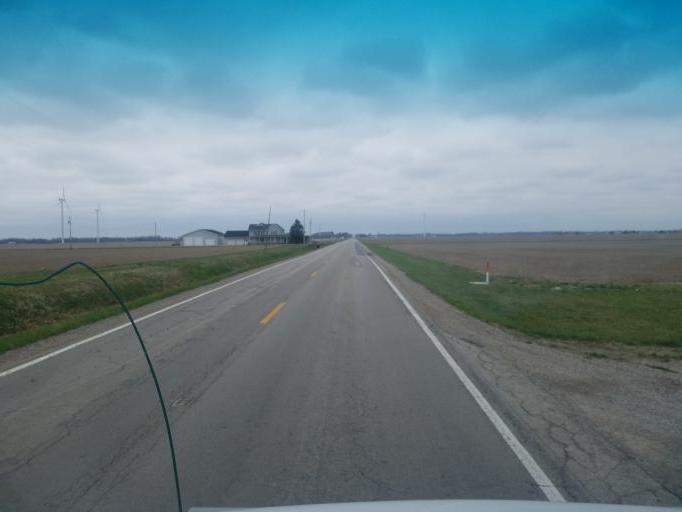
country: US
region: Ohio
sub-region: Paulding County
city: Payne
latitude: 41.0390
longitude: -84.7267
